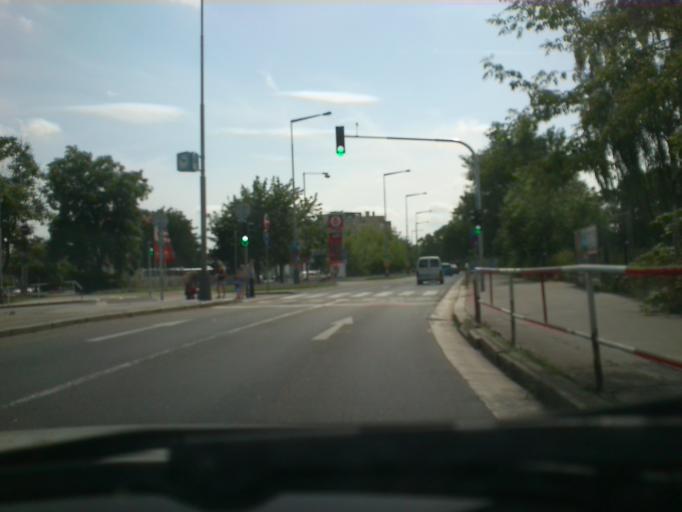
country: CZ
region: Praha
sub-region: Praha 8
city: Karlin
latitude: 50.1012
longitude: 14.4432
